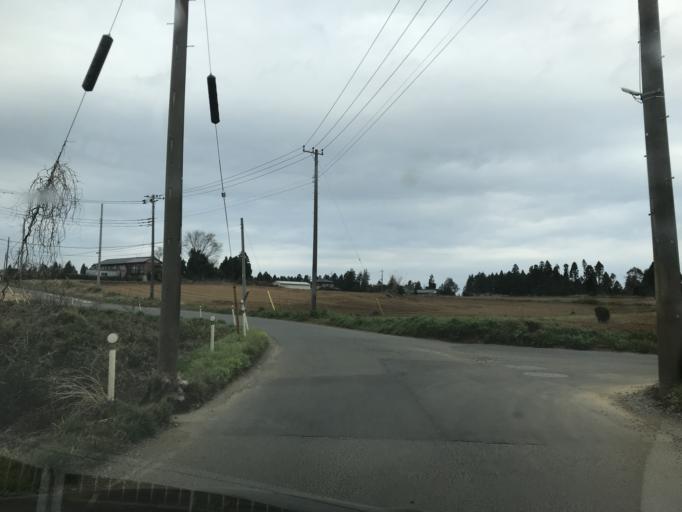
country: JP
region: Chiba
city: Sawara
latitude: 35.8504
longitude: 140.4762
